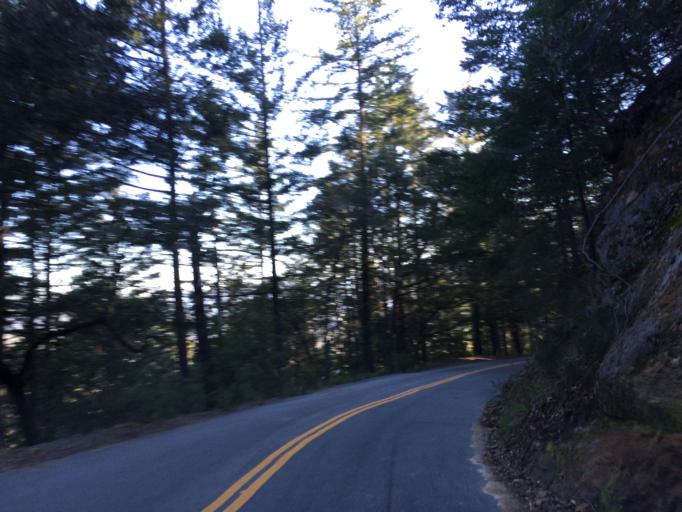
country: US
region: California
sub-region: Santa Cruz County
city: Boulder Creek
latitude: 37.1468
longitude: -122.1802
